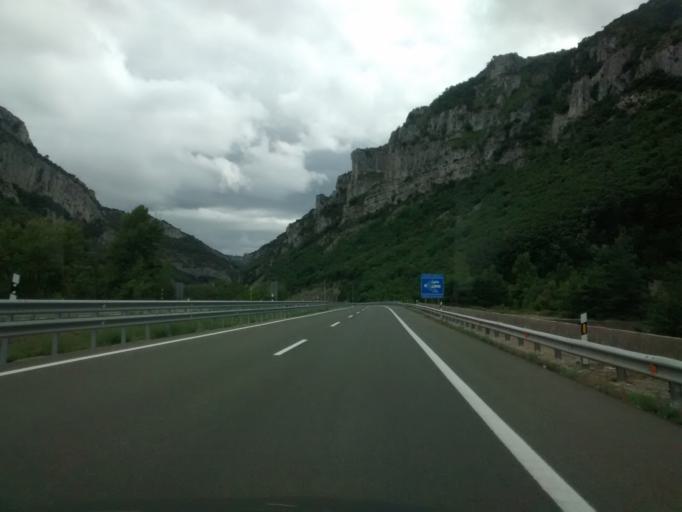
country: ES
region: Basque Country
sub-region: Provincia de Alava
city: Arminon
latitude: 42.8433
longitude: -2.8935
